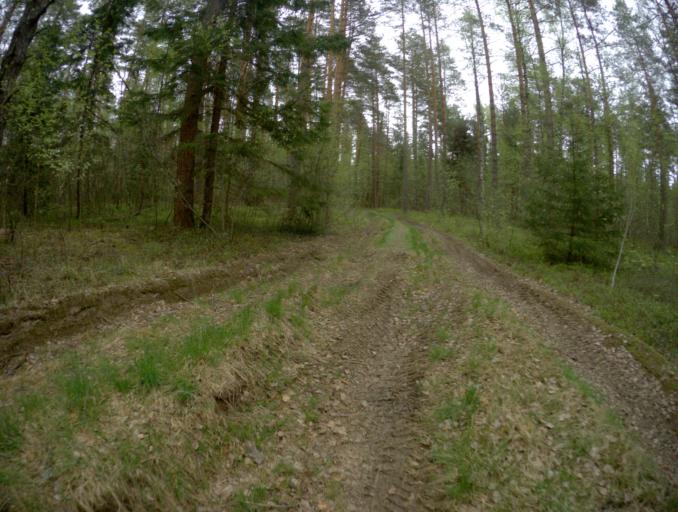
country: RU
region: Vladimir
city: Golovino
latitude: 55.9045
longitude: 40.4613
